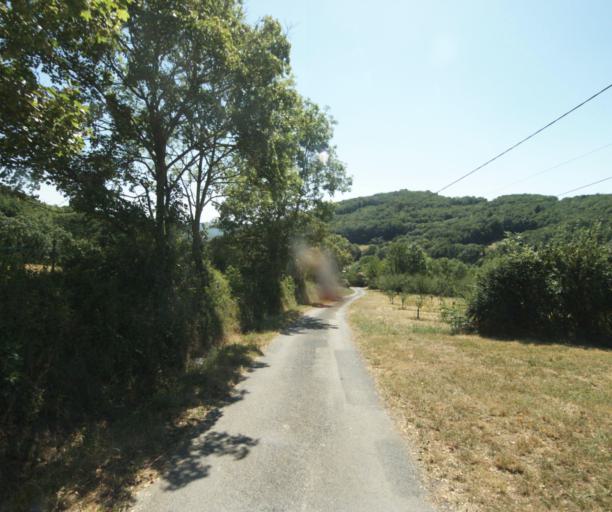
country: FR
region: Rhone-Alpes
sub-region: Departement du Rhone
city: Bessenay
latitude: 45.7922
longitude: 4.5254
